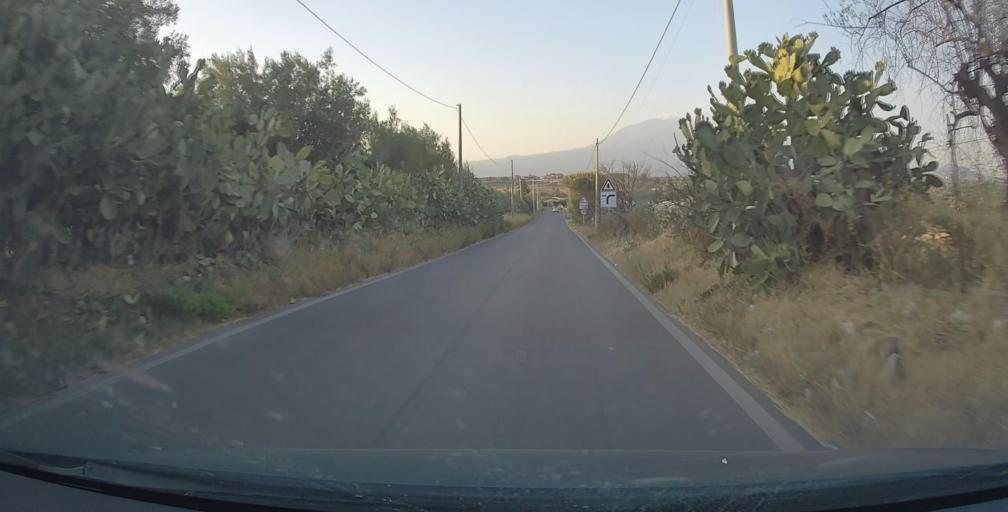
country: IT
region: Sicily
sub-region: Catania
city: Palazzolo
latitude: 37.5440
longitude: 14.9302
